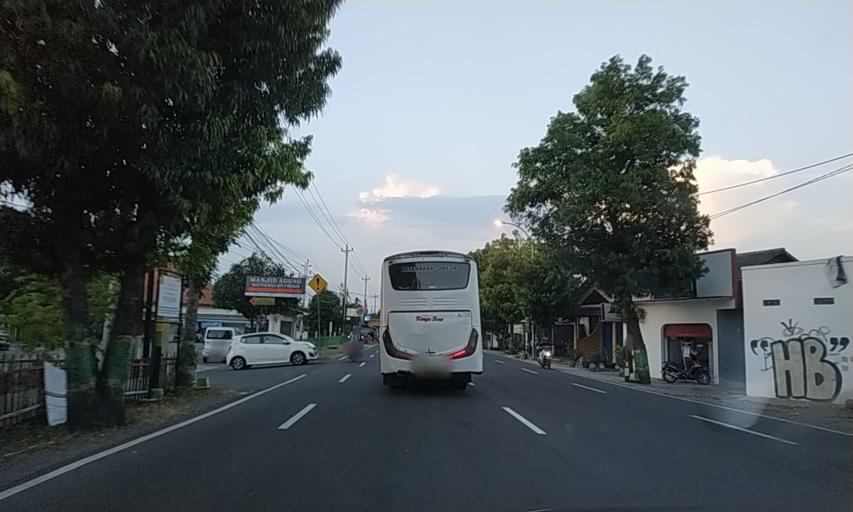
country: ID
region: Daerah Istimewa Yogyakarta
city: Srandakan
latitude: -7.8680
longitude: 110.1489
